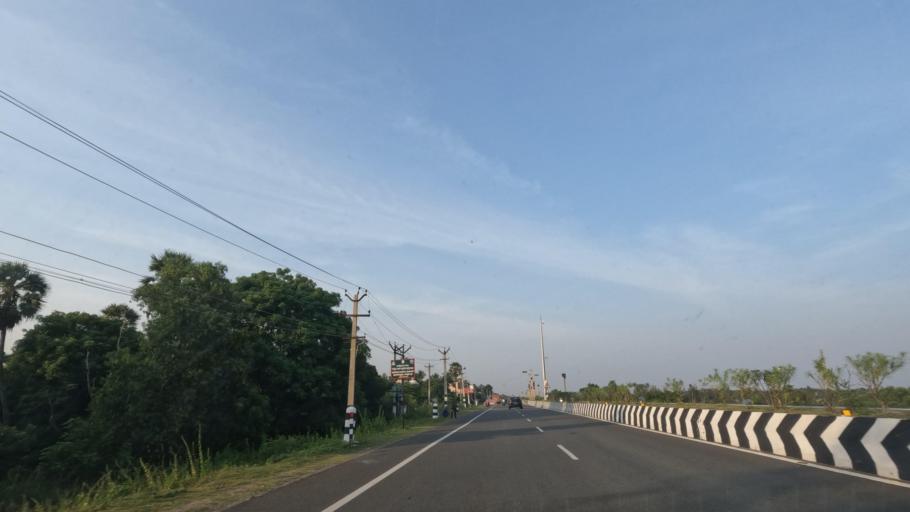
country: IN
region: Tamil Nadu
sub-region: Kancheepuram
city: Mamallapuram
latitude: 12.7159
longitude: 80.2271
